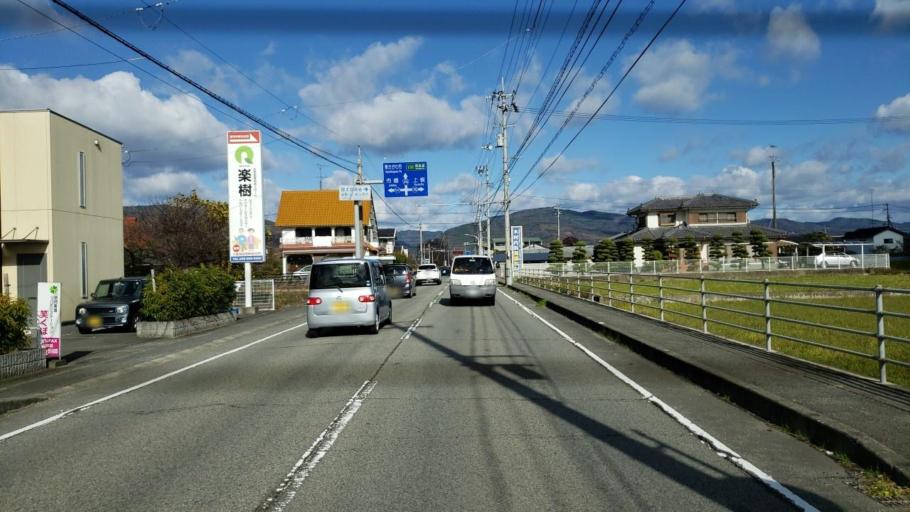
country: JP
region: Tokushima
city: Kamojimacho-jogejima
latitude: 34.0948
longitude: 134.3438
